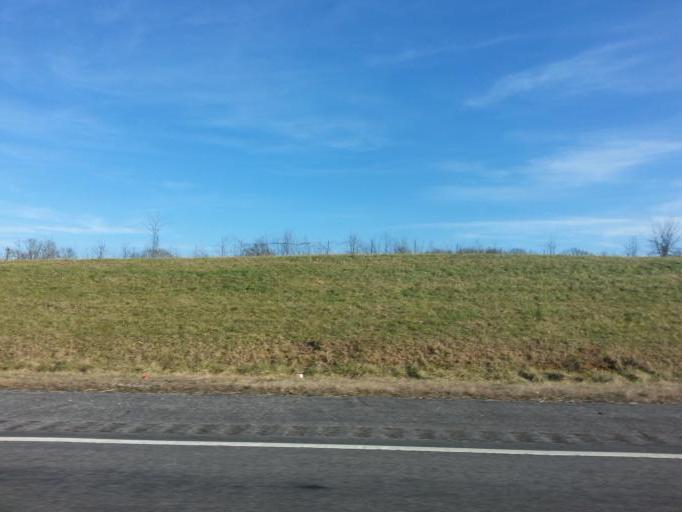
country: US
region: Tennessee
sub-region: Warren County
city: McMinnville
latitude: 35.7347
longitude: -85.6594
